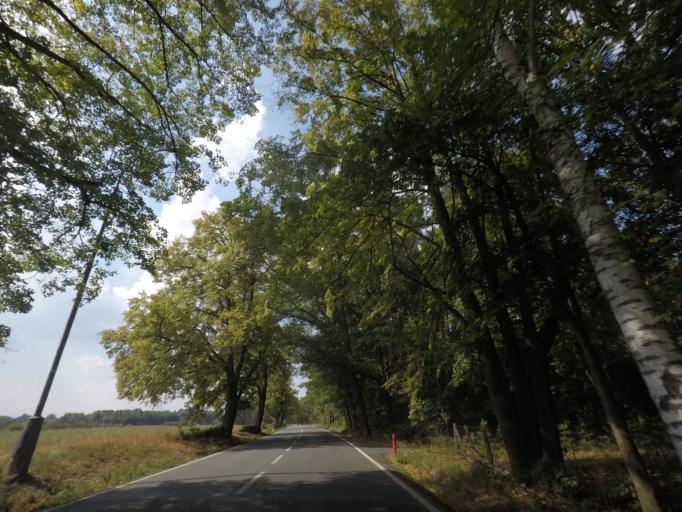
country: CZ
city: Albrechtice nad Orlici
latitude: 50.1236
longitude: 16.0675
